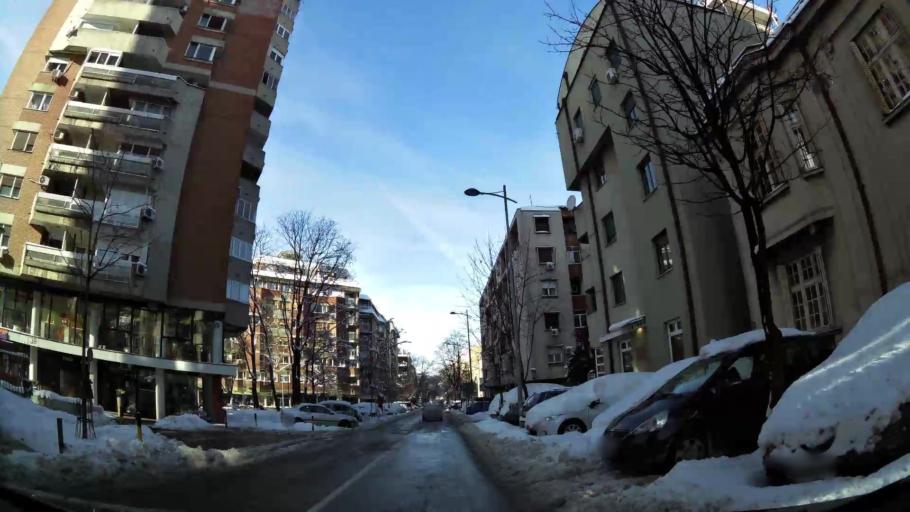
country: RS
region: Central Serbia
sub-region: Belgrade
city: Vracar
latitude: 44.7993
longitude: 20.4814
